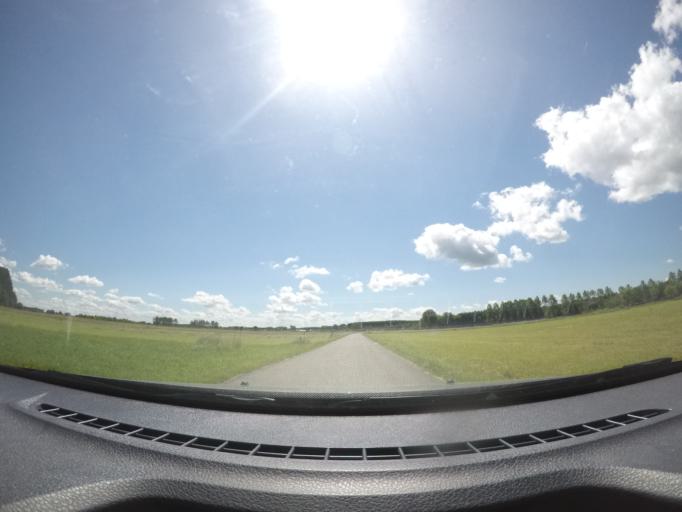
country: BE
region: Wallonia
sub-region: Province du Luxembourg
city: Tintigny
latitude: 49.6770
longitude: 5.5176
